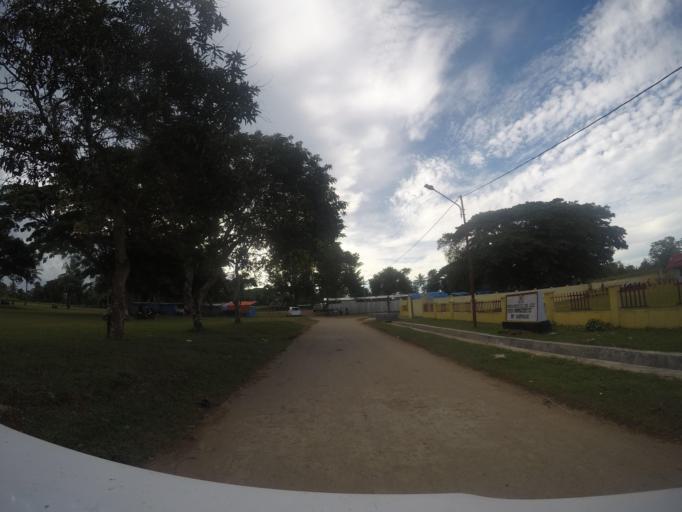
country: TL
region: Lautem
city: Lospalos
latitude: -8.5063
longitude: 126.9871
